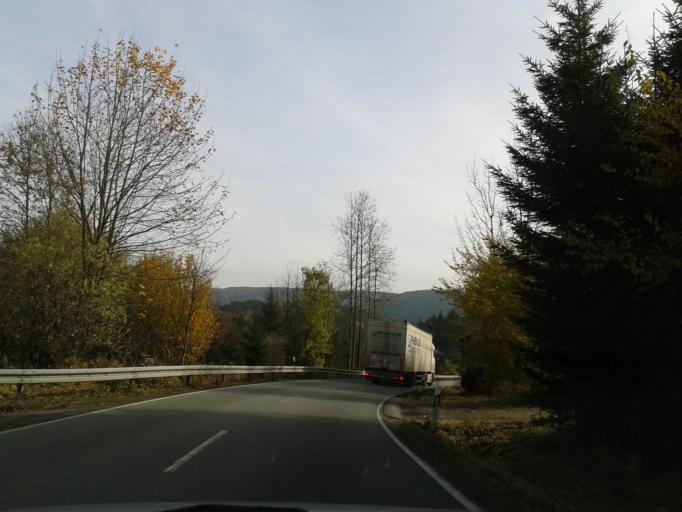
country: DE
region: North Rhine-Westphalia
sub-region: Regierungsbezirk Arnsberg
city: Bestwig
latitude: 51.3912
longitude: 8.4149
